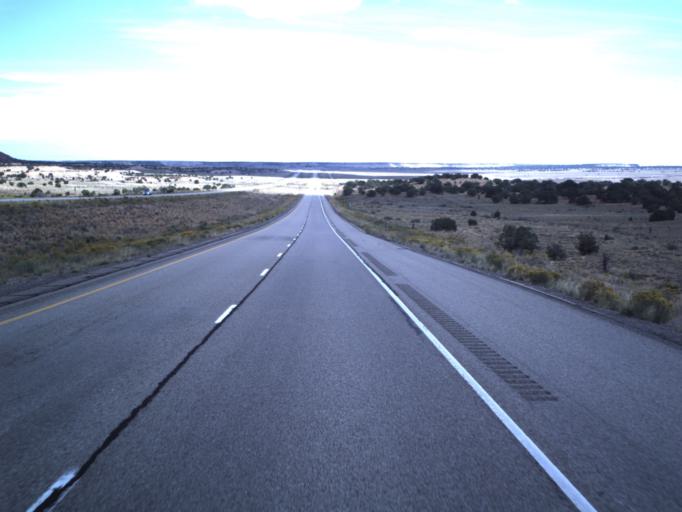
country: US
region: Utah
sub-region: Emery County
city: Castle Dale
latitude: 38.8674
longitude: -110.7047
